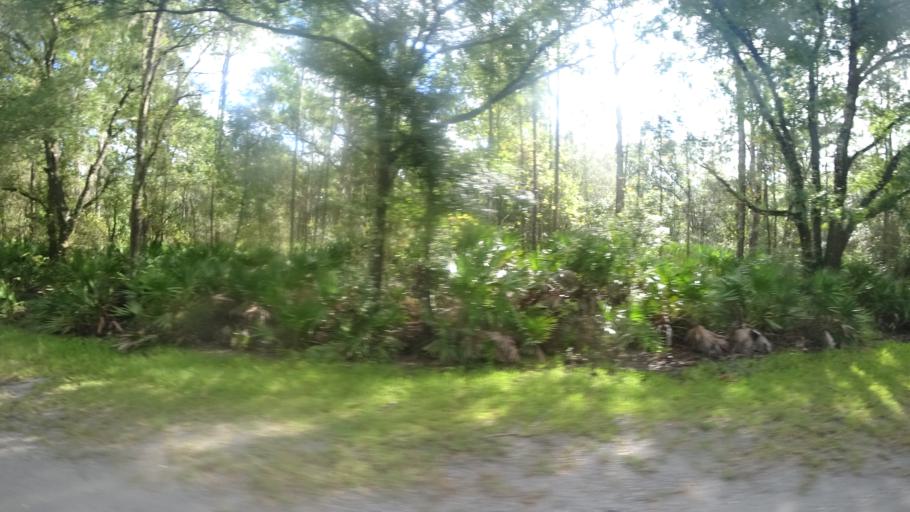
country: US
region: Florida
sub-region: Hillsborough County
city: Sun City Center
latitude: 27.5987
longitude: -82.3638
